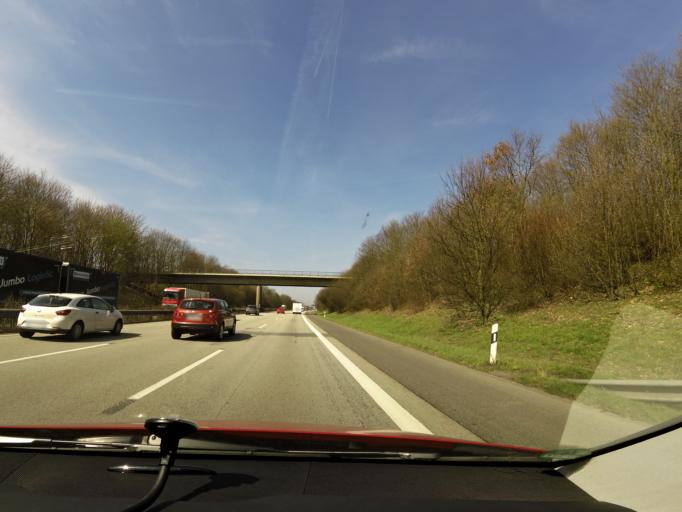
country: DE
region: Rheinland-Pfalz
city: Bad Neuenahr-Ahrweiler
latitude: 50.5765
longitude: 7.0767
